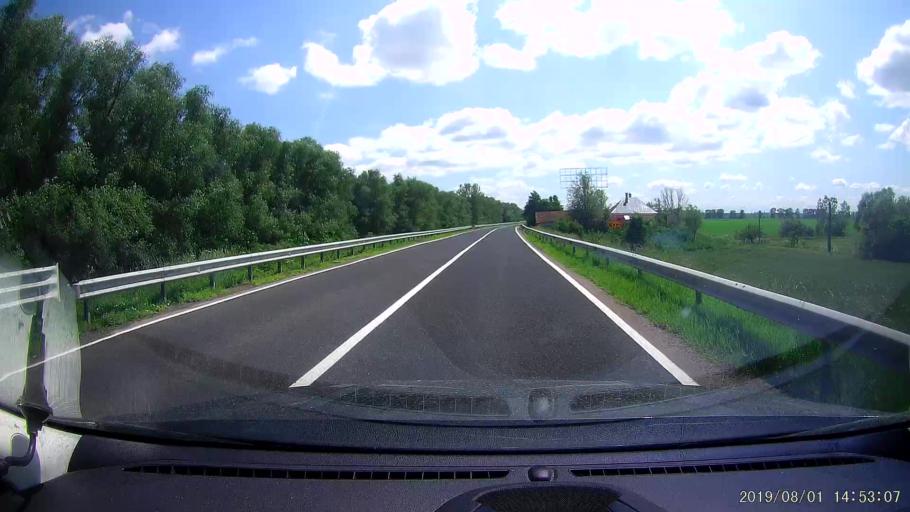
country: RO
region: Braila
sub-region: Comuna Vadeni
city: Vadeni
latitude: 45.3425
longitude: 28.0066
